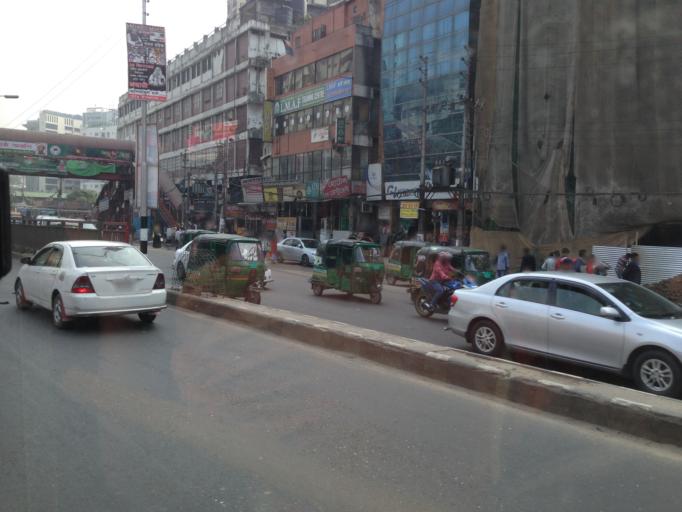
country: BD
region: Dhaka
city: Azimpur
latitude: 23.7783
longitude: 90.3604
